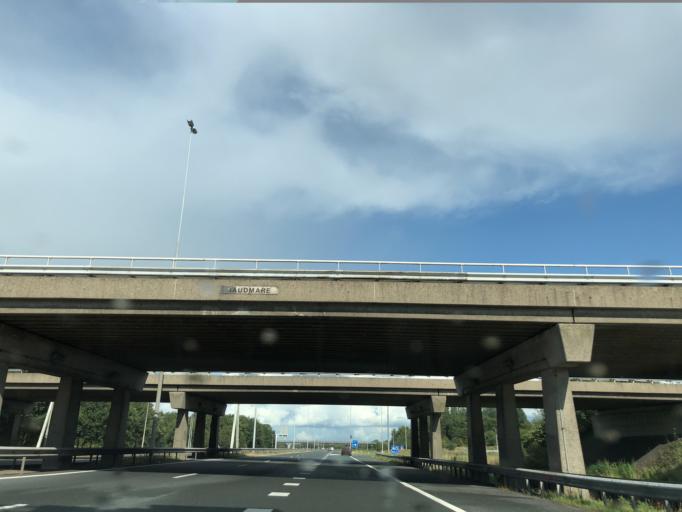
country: NL
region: Friesland
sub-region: Gemeente Smallingerland
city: Drachtstercompagnie
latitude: 53.1046
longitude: 6.1339
